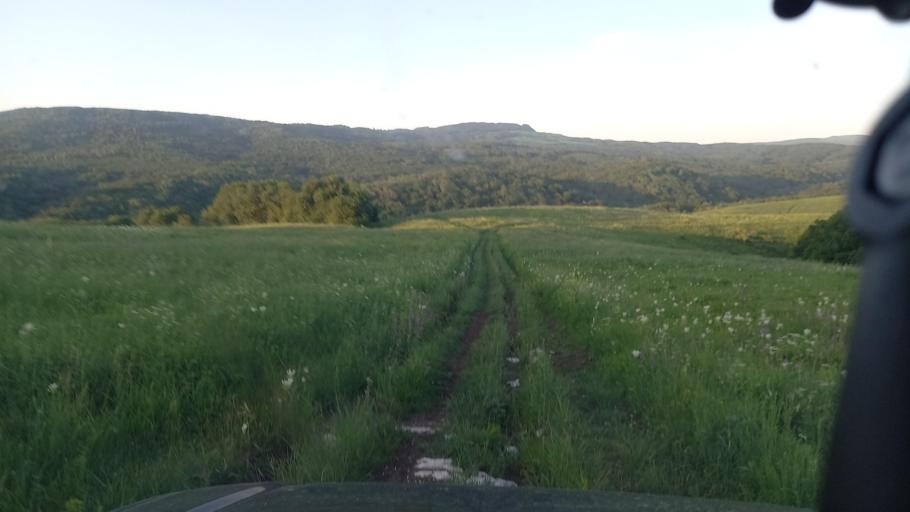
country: RU
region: Karachayevo-Cherkesiya
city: Pregradnaya
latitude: 44.1257
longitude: 41.0999
